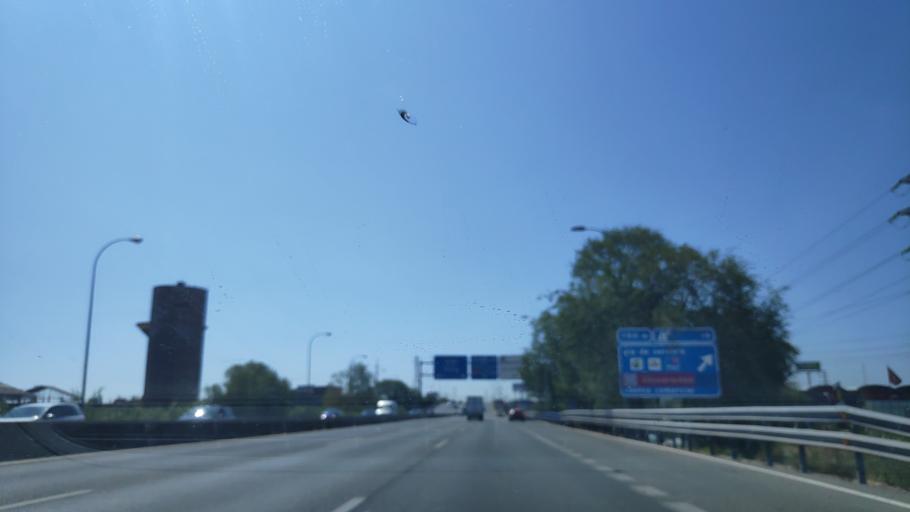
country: ES
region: Madrid
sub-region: Provincia de Madrid
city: Villaverde
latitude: 40.3412
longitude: -3.7241
